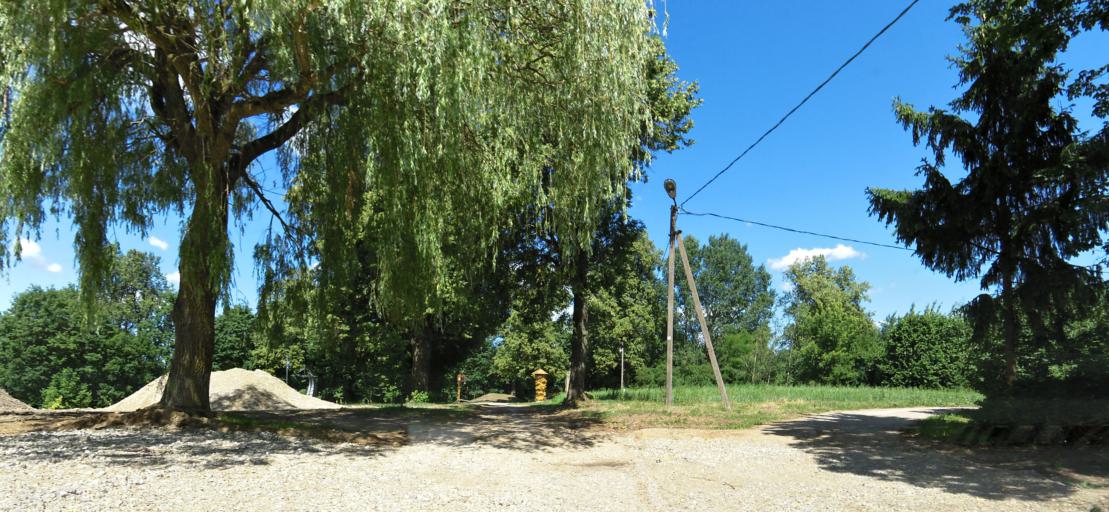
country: LT
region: Panevezys
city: Pasvalys
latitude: 56.2297
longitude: 24.4170
